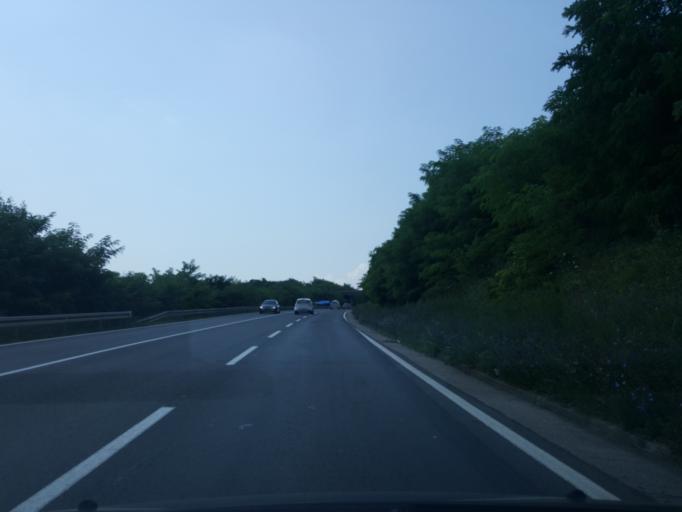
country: RS
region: Central Serbia
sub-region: Belgrade
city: Sopot
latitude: 44.5408
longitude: 20.6588
